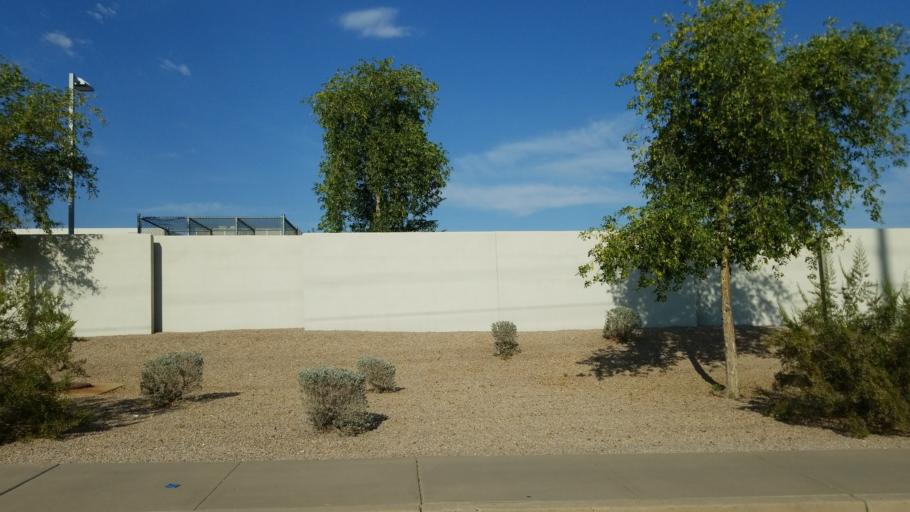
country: US
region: Arizona
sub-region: Maricopa County
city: Tempe
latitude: 33.4498
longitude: -111.9179
